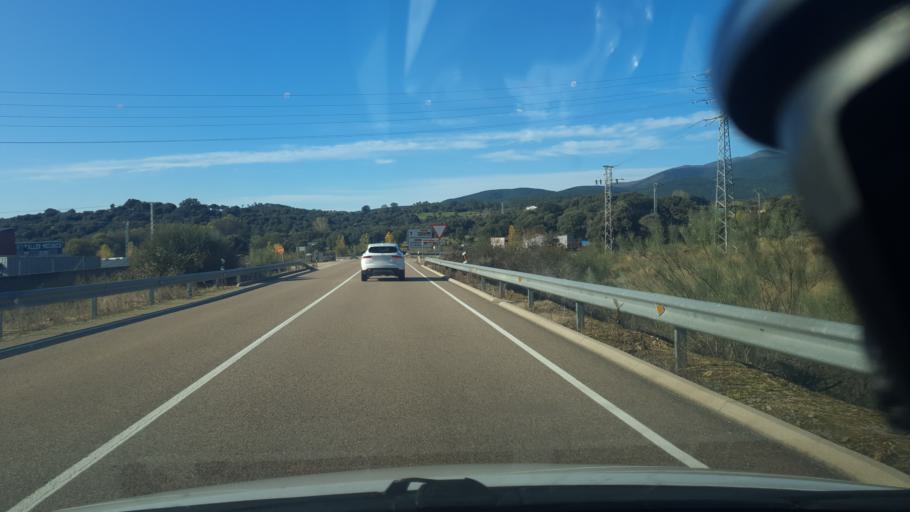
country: ES
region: Castille and Leon
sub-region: Provincia de Avila
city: Arenas de San Pedro
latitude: 40.1855
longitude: -5.0498
